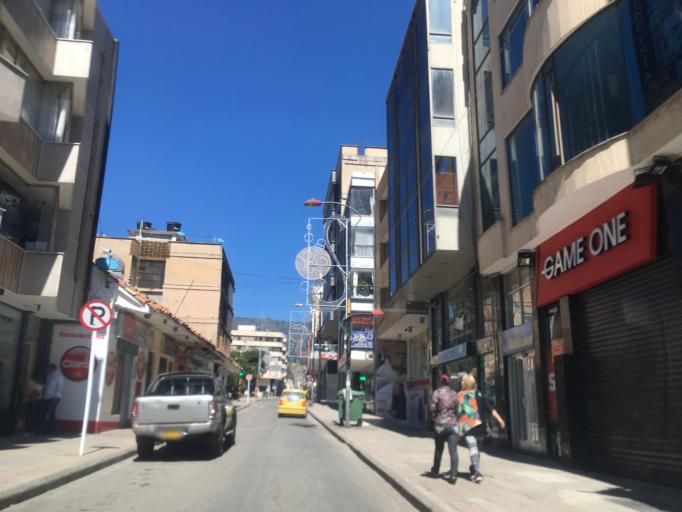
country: CO
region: Boyaca
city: Duitama
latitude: 5.8270
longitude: -73.0330
